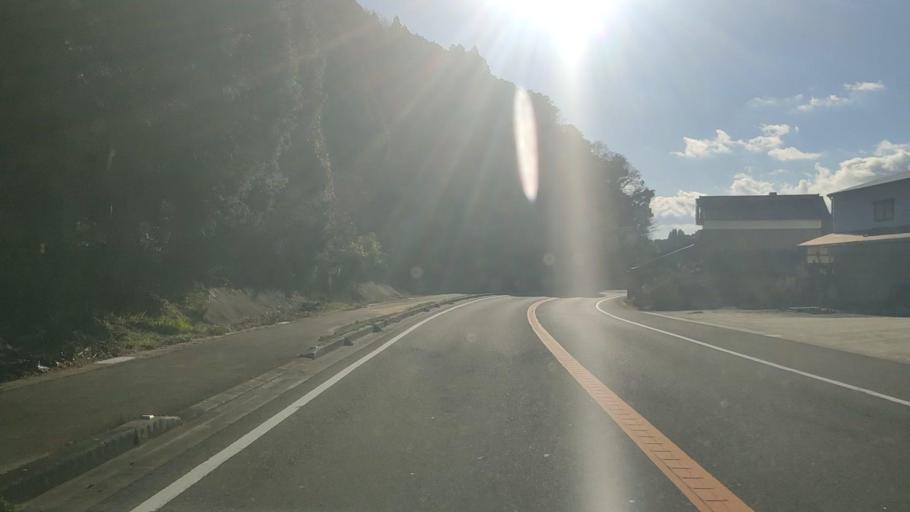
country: JP
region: Fukuoka
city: Maebaru-chuo
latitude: 33.4401
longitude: 130.2665
